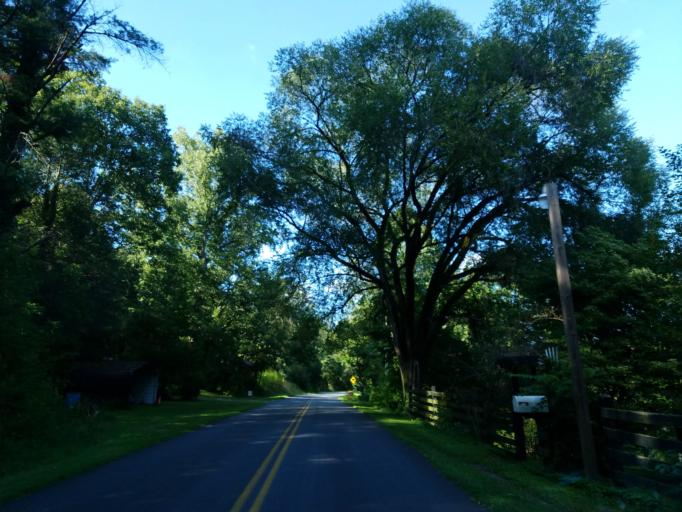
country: US
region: Georgia
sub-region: Fannin County
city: Blue Ridge
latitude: 34.7394
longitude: -84.2270
